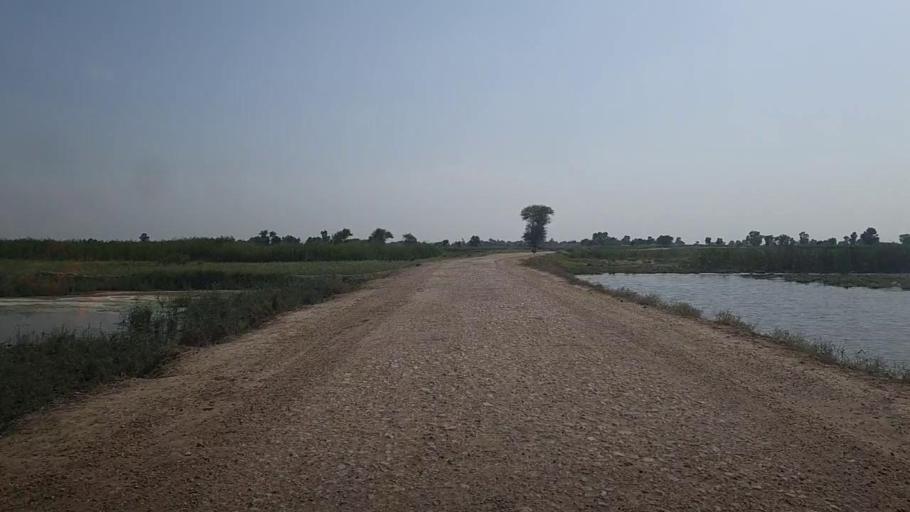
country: PK
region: Sindh
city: Ubauro
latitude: 28.1474
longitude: 69.8037
